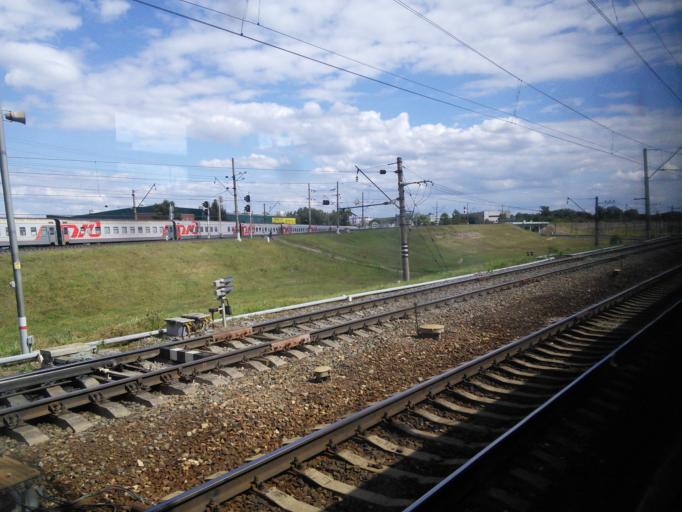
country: RU
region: Moscow
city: Nekrasovka
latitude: 55.6733
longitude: 37.9144
